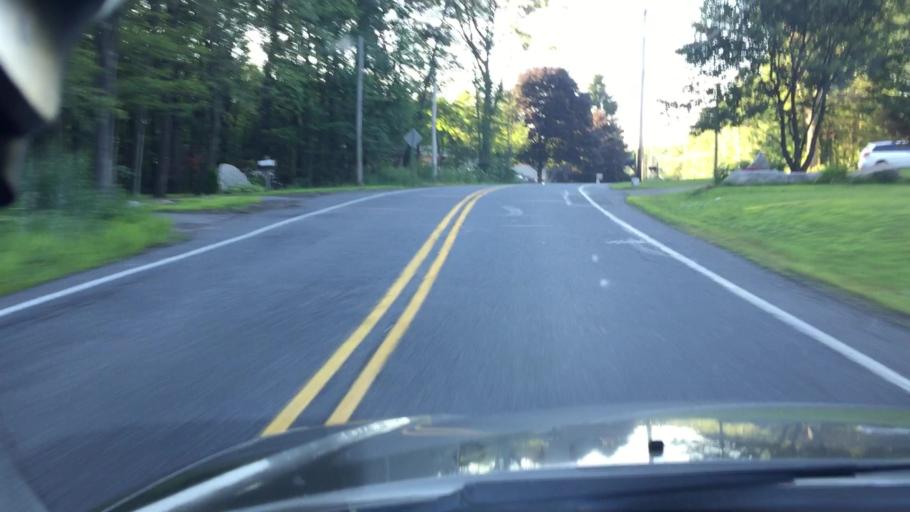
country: US
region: Pennsylvania
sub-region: Luzerne County
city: Harleigh
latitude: 40.9841
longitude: -75.9753
